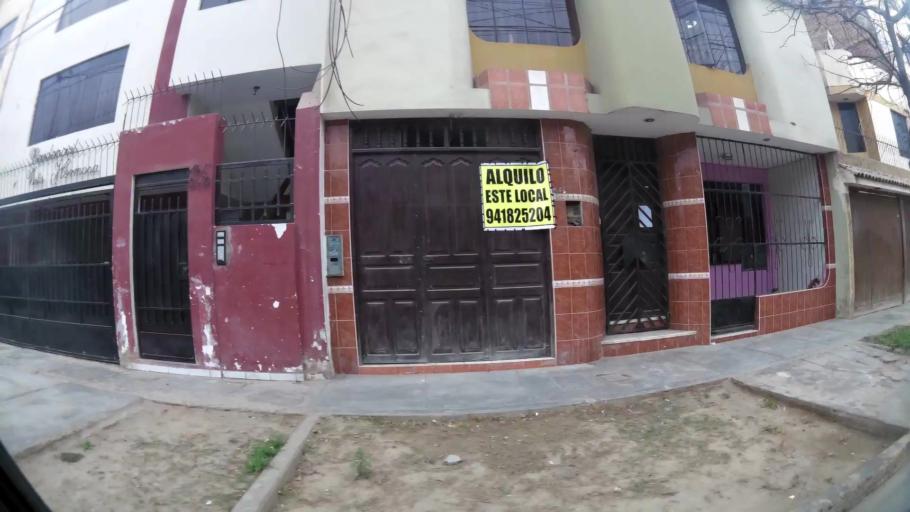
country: PE
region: La Libertad
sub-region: Provincia de Trujillo
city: Trujillo
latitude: -8.1209
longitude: -79.0425
